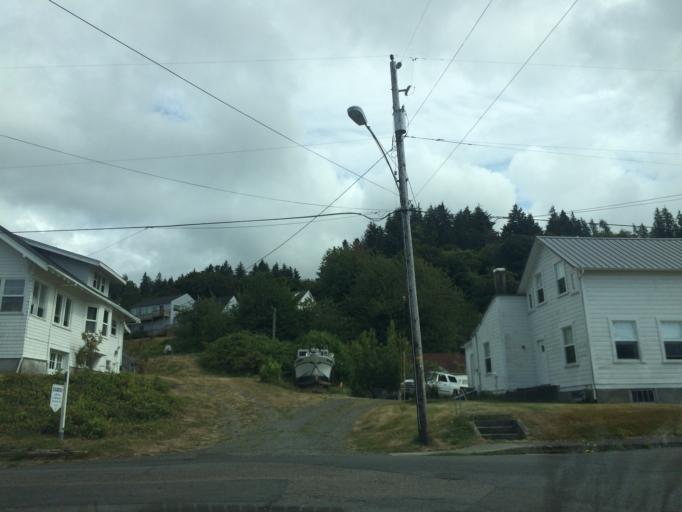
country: US
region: Oregon
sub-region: Clatsop County
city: Astoria
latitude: 46.1903
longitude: -123.8088
